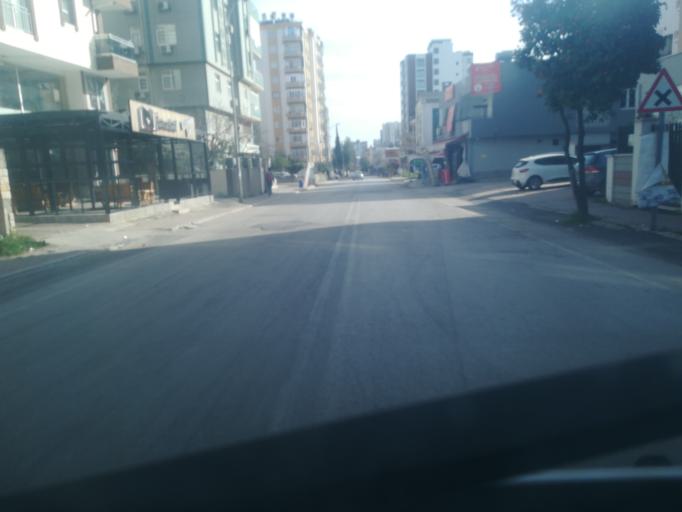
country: TR
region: Adana
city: Adana
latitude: 37.0374
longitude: 35.3125
